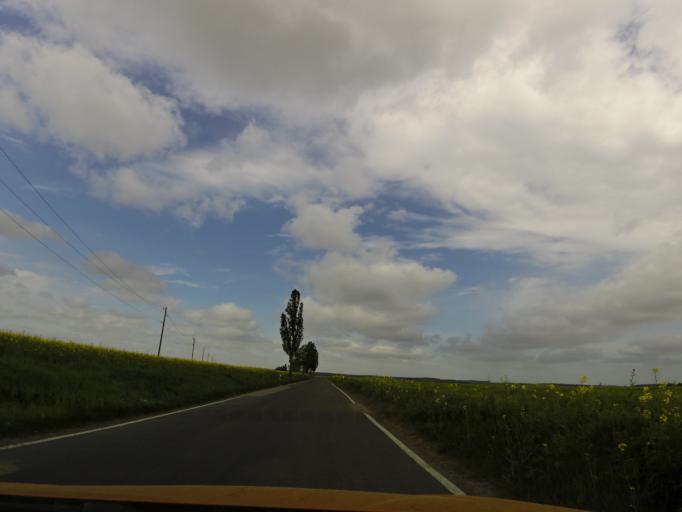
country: DE
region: Brandenburg
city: Niemegk
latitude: 52.1000
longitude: 12.6587
